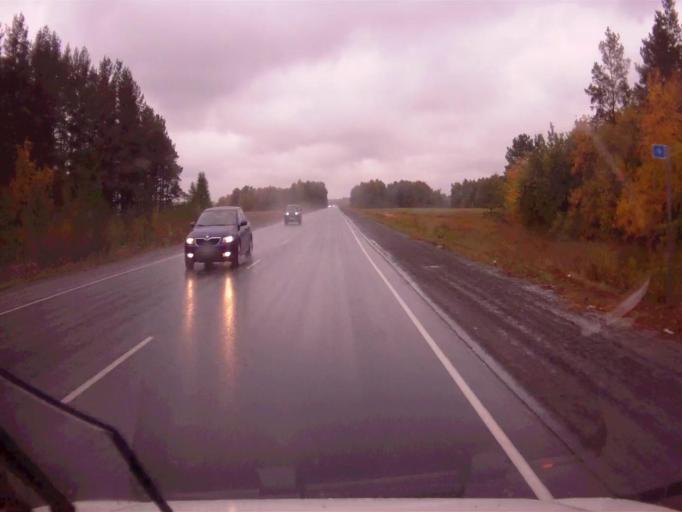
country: RU
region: Chelyabinsk
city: Roshchino
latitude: 55.3844
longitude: 61.1345
